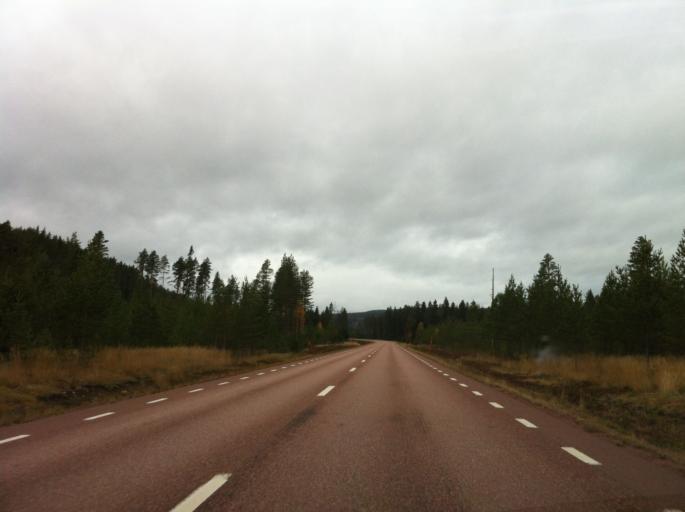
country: SE
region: Dalarna
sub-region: Alvdalens Kommun
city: AElvdalen
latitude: 61.2765
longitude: 13.8918
